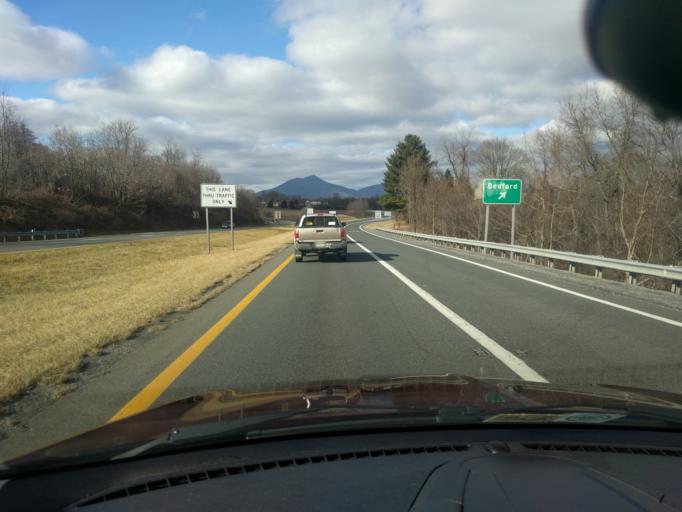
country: US
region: Virginia
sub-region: City of Bedford
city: Bedford
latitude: 37.3322
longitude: -79.5426
